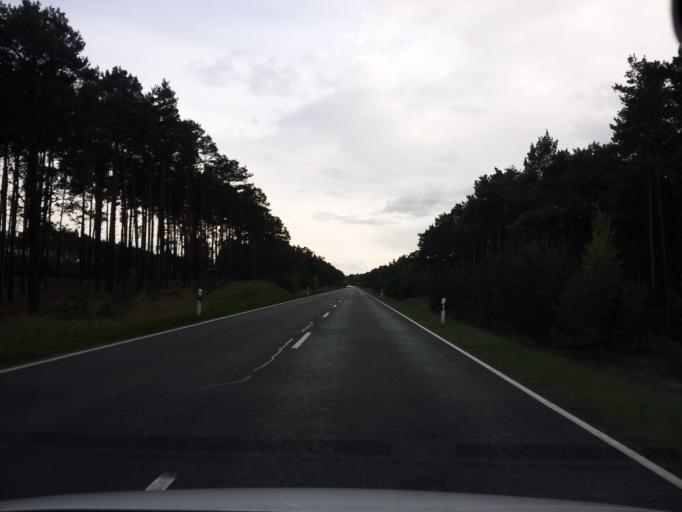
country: DE
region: Brandenburg
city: Janschwalde
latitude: 51.8559
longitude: 14.5177
